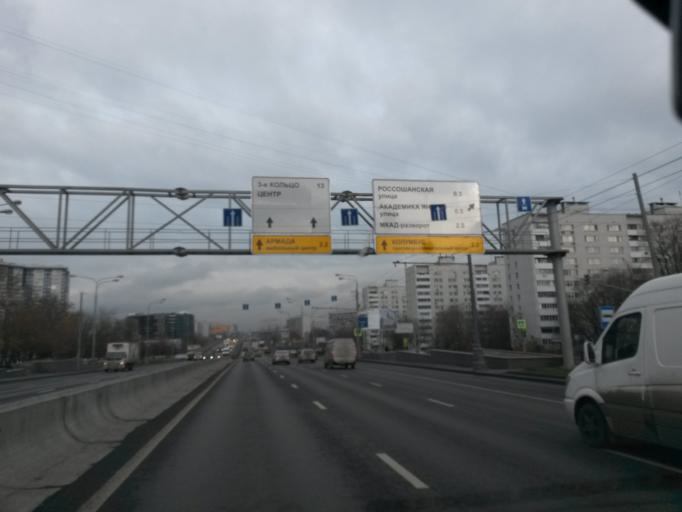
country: RU
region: Moscow
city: Chertanovo Yuzhnoye
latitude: 55.5917
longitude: 37.6004
